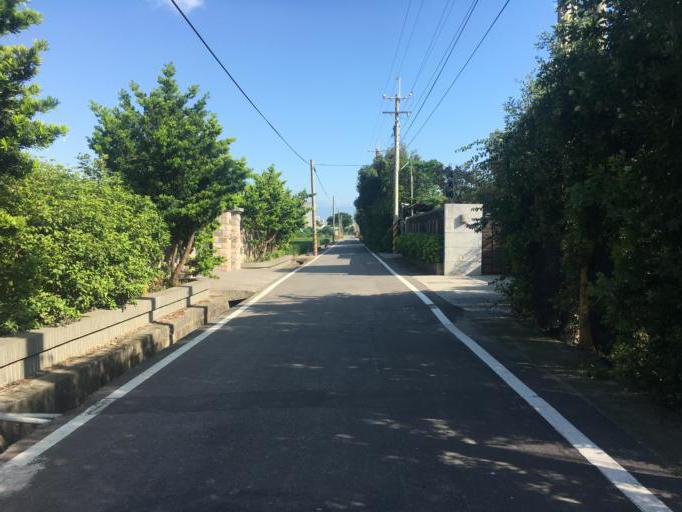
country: TW
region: Taiwan
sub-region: Hsinchu
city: Zhubei
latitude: 24.8402
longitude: 120.9880
